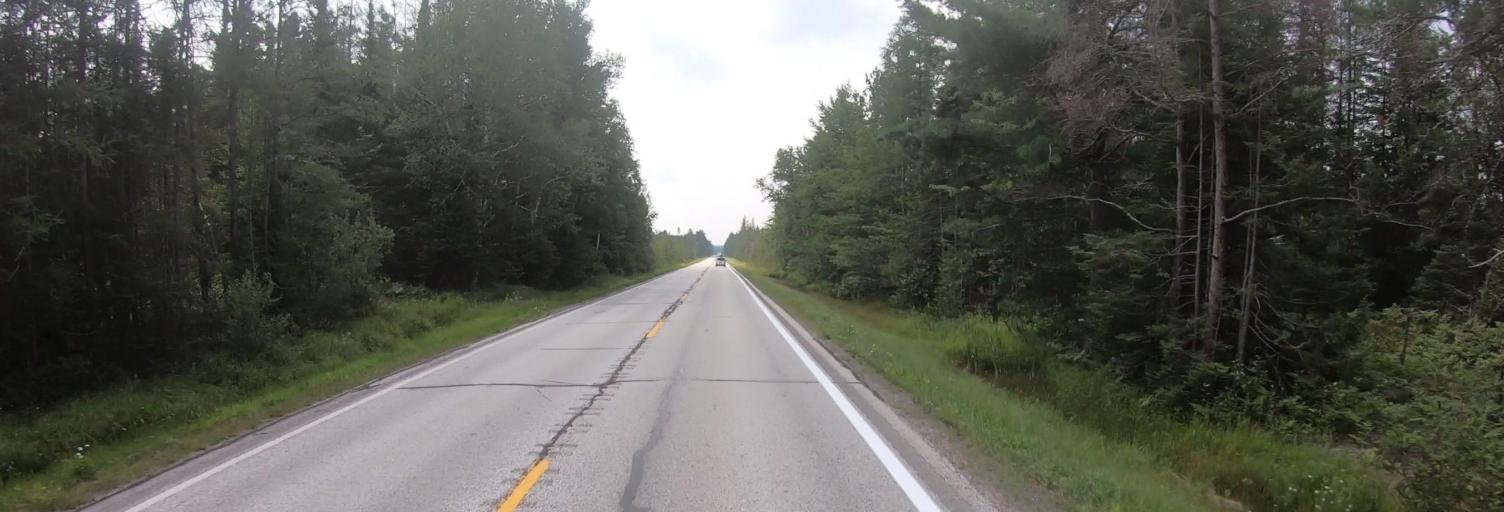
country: US
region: Michigan
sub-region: Luce County
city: Newberry
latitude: 46.4898
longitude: -85.4268
